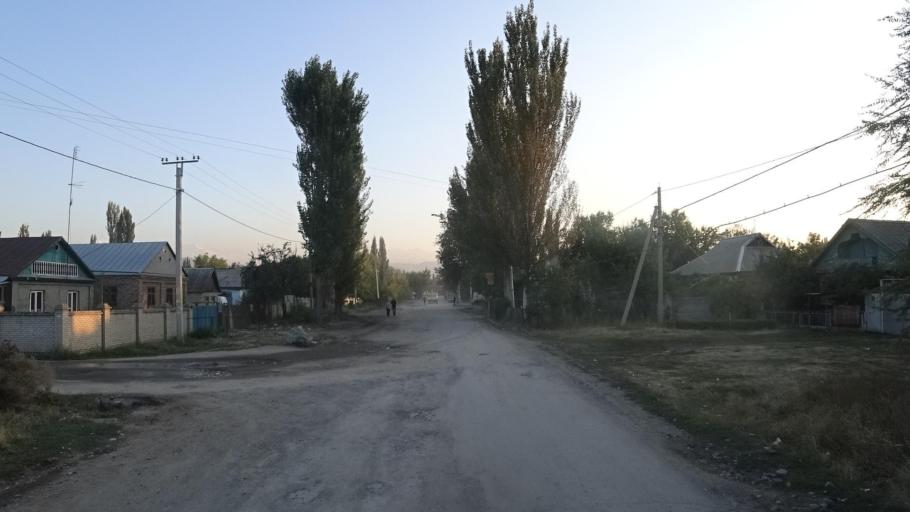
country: KG
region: Chuy
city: Lebedinovka
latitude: 42.8762
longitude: 74.7192
